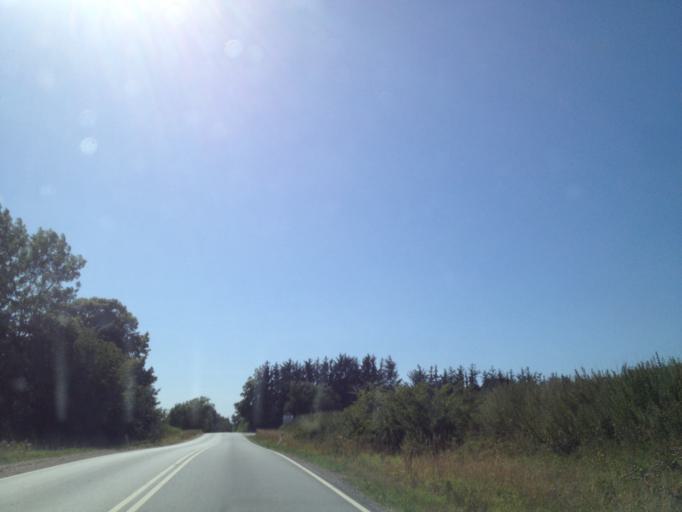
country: DK
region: Capital Region
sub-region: Helsingor Kommune
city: Hornbaek
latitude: 56.0431
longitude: 12.4266
